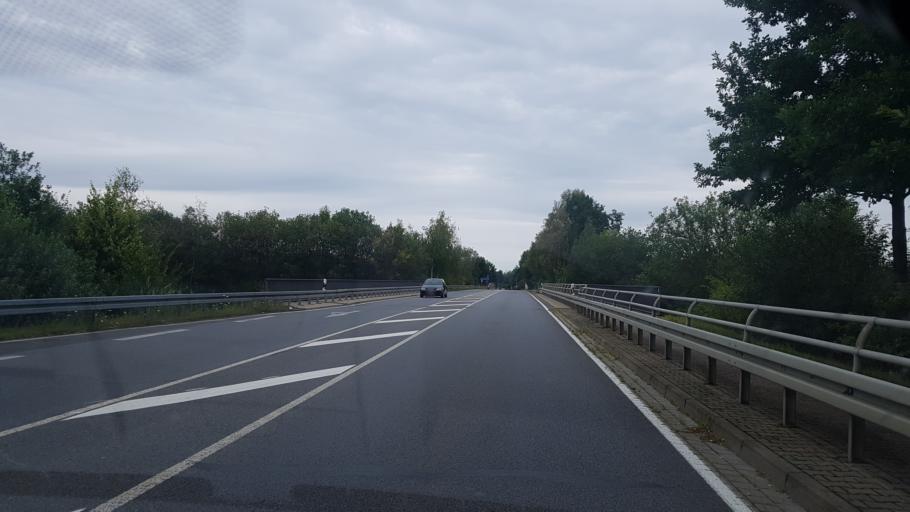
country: DE
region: Saxony
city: Ohorn
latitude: 51.1641
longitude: 14.0517
